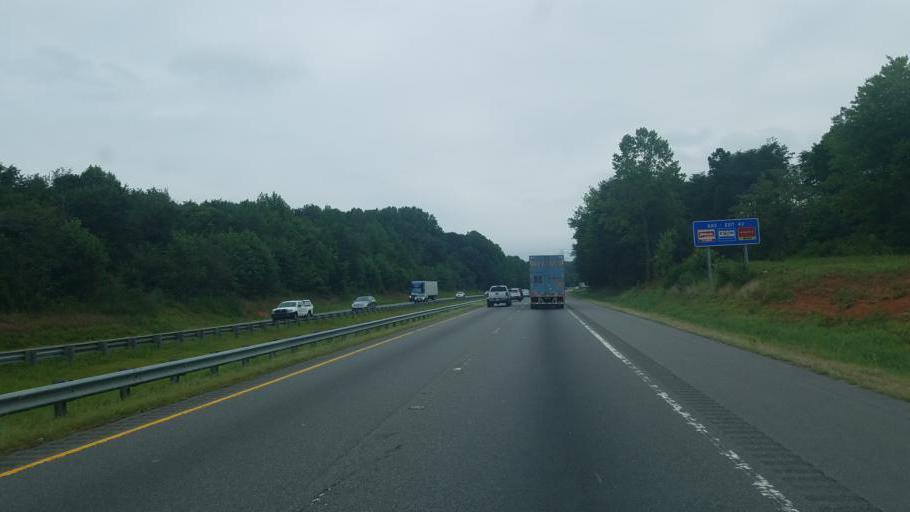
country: US
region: North Carolina
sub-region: Iredell County
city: Troutman
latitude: 35.6642
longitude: -80.8597
